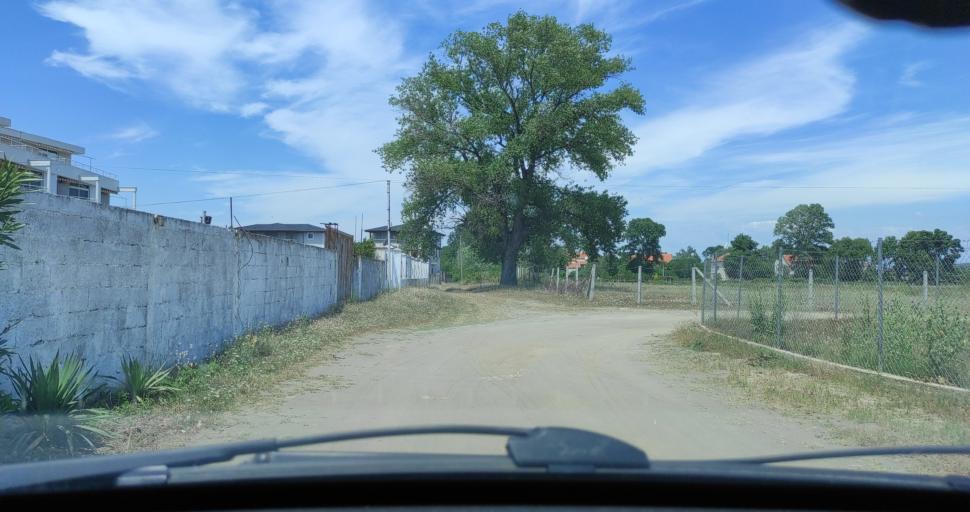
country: AL
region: Shkoder
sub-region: Rrethi i Shkodres
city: Velipoje
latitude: 41.8684
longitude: 19.4018
